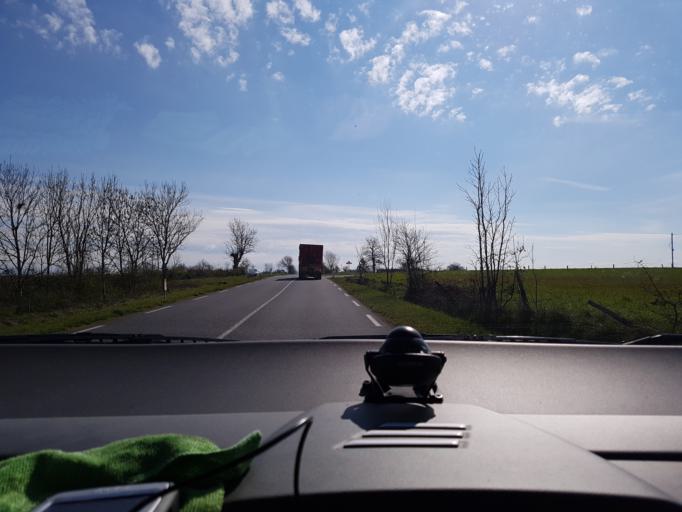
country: FR
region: Midi-Pyrenees
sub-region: Departement de l'Aveyron
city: Druelle
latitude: 44.3700
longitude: 2.4711
